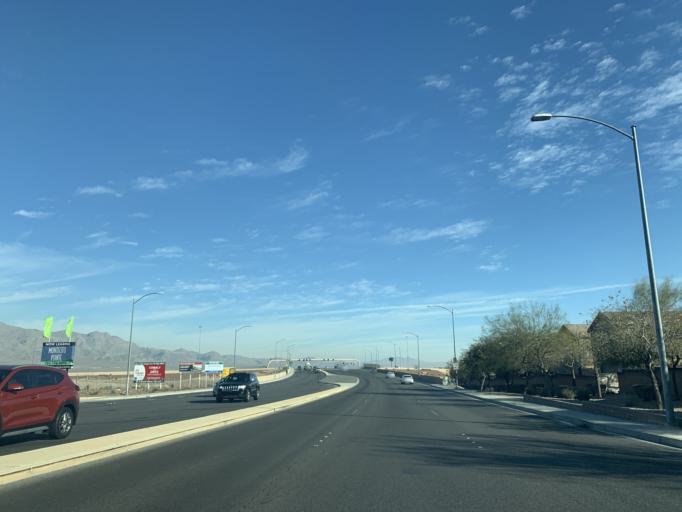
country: US
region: Nevada
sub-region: Clark County
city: Summerlin South
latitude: 36.3140
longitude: -115.3048
